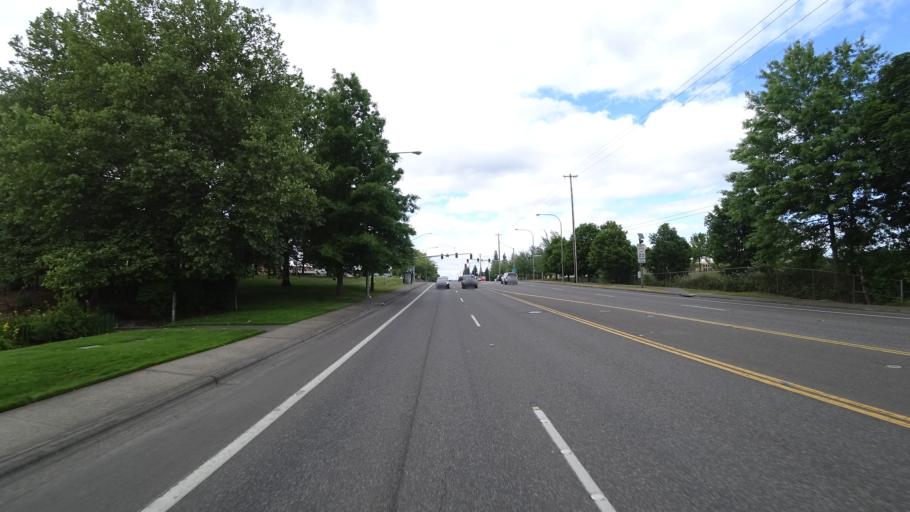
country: US
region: Oregon
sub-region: Washington County
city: Rockcreek
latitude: 45.5481
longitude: -122.8676
